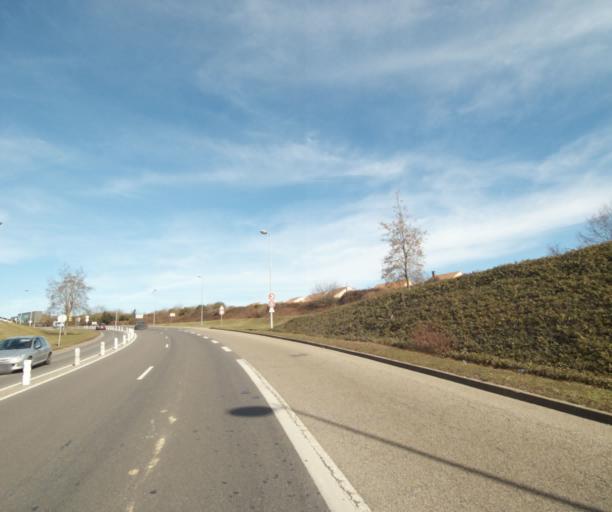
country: FR
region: Lorraine
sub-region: Departement de Meurthe-et-Moselle
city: Laxou
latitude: 48.6900
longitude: 6.1334
